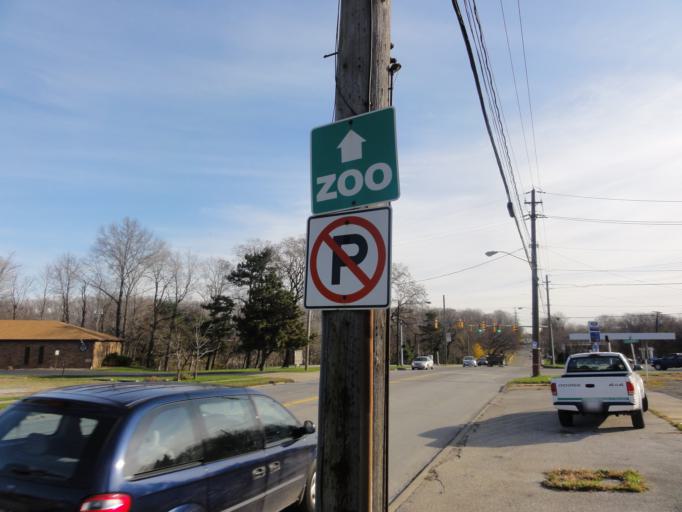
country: US
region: Ohio
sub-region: Cuyahoga County
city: Brooklyn
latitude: 41.4400
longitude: -81.7563
